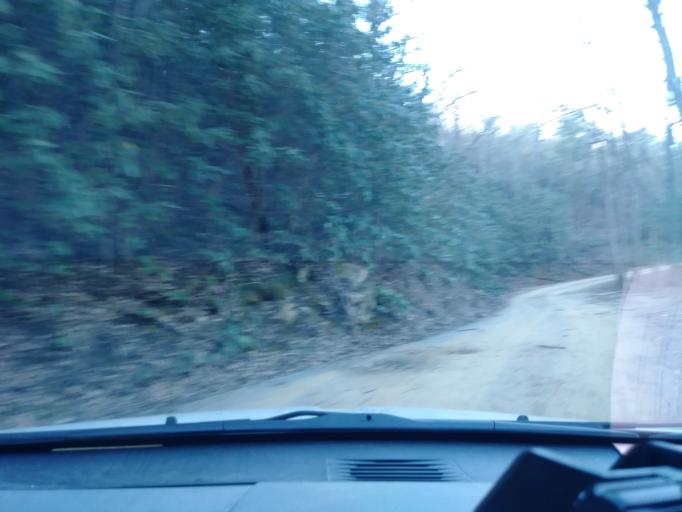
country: US
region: Tennessee
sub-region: Greene County
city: Tusculum
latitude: 36.0764
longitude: -82.6869
